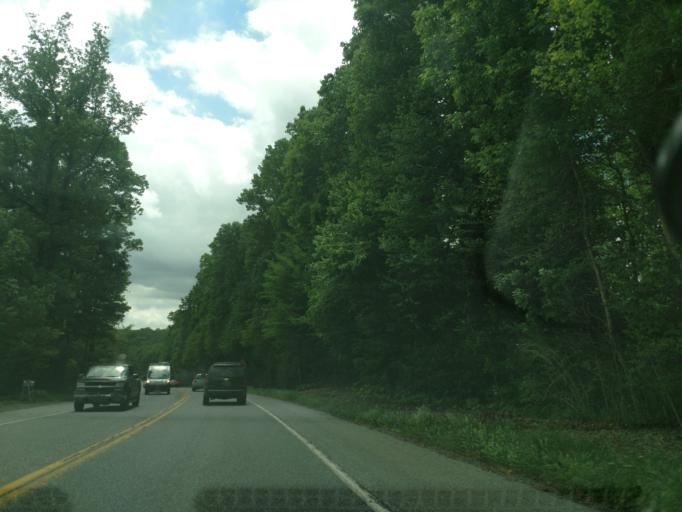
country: US
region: Pennsylvania
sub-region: Lebanon County
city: Cornwall
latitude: 40.2502
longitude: -76.4350
